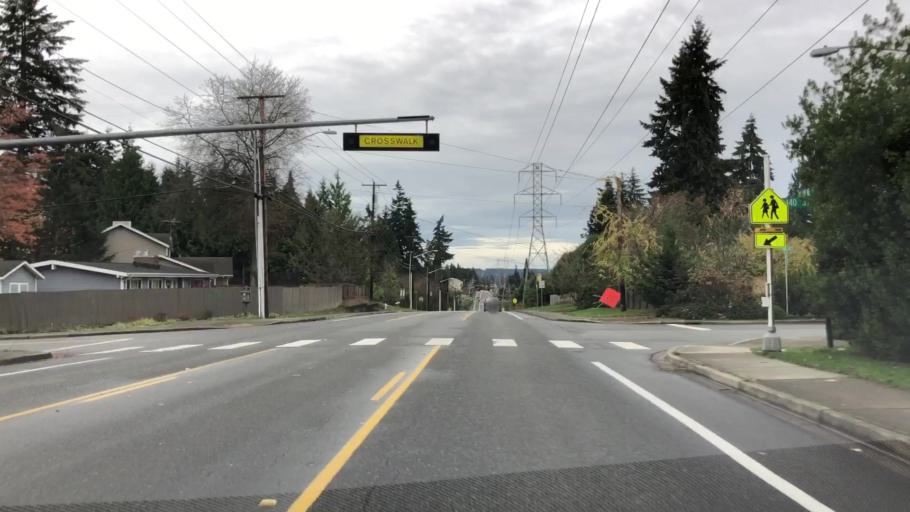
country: US
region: Washington
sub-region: King County
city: Kingsgate
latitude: 47.7261
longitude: -122.1756
